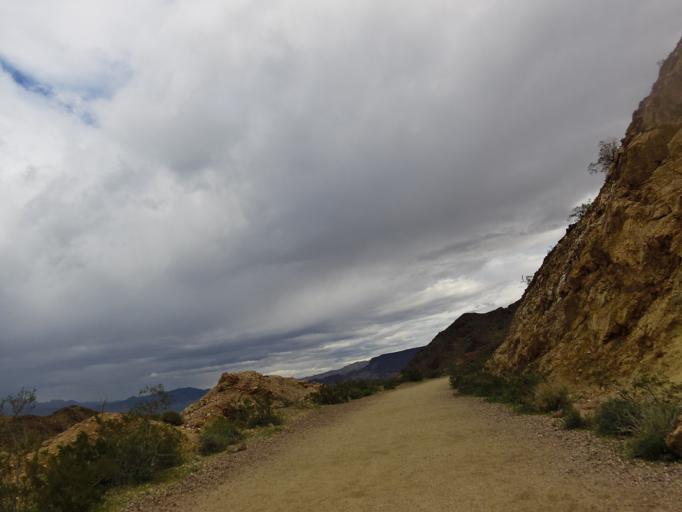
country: US
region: Nevada
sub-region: Clark County
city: Boulder City
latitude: 36.0129
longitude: -114.7886
